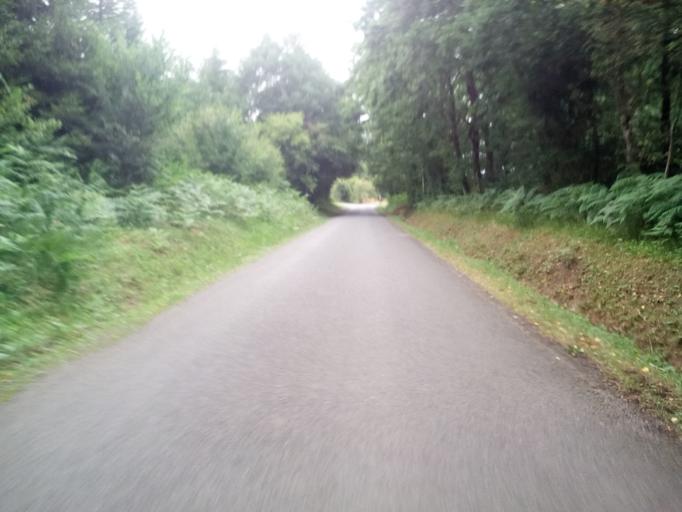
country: FR
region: Lower Normandy
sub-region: Departement du Calvados
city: Clinchamps-sur-Orne
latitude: 49.0303
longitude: -0.3943
